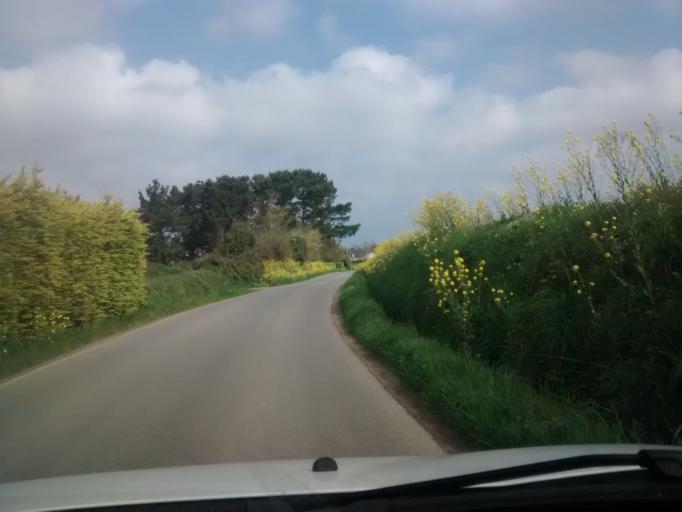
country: FR
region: Brittany
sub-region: Departement des Cotes-d'Armor
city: Penvenan
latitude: 48.8208
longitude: -3.3052
